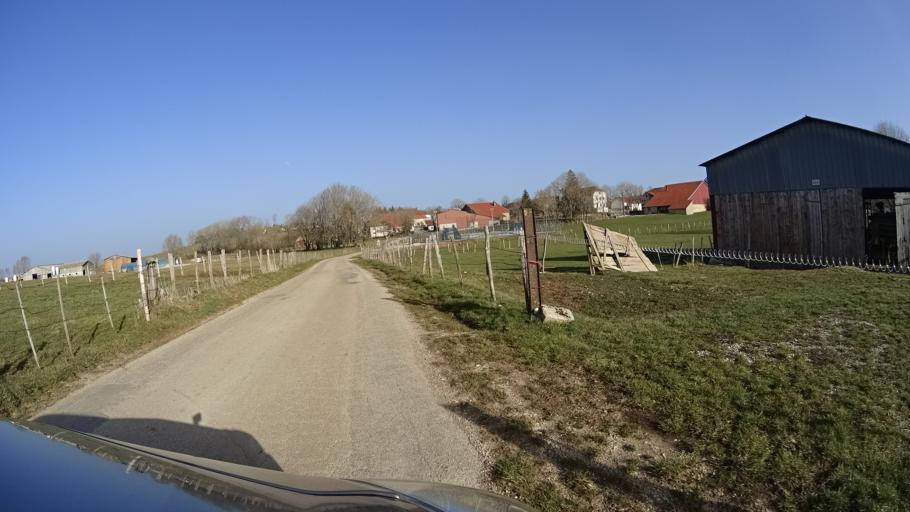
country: FR
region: Franche-Comte
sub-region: Departement du Doubs
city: Frasne
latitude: 46.8948
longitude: 6.2198
